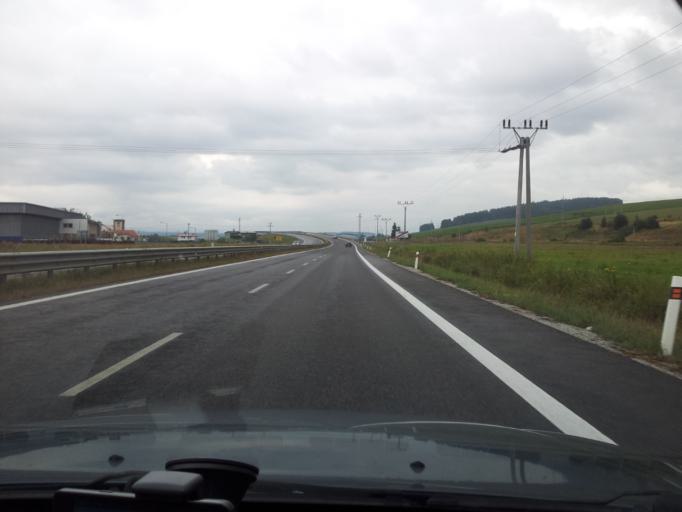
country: SK
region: Presovsky
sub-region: Okres Poprad
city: Poprad
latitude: 49.0771
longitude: 20.3307
